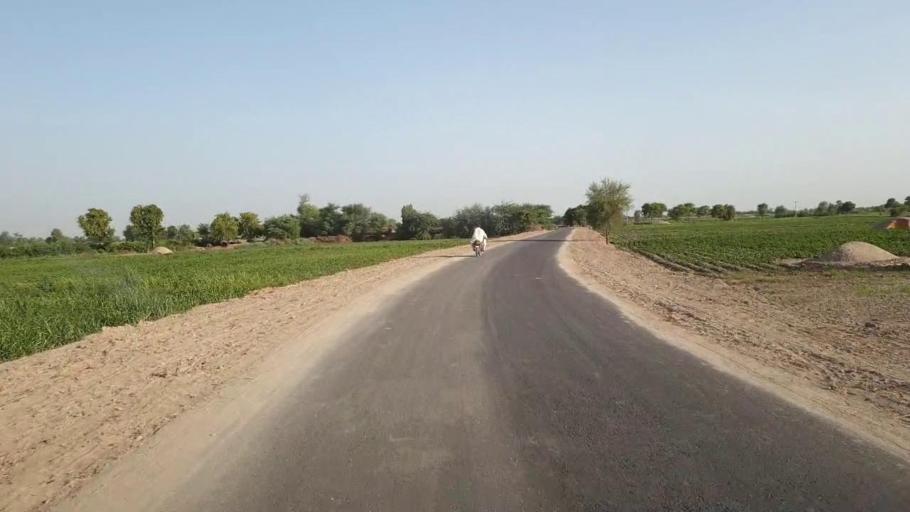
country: PK
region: Sindh
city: Jam Sahib
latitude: 26.3438
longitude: 68.5689
